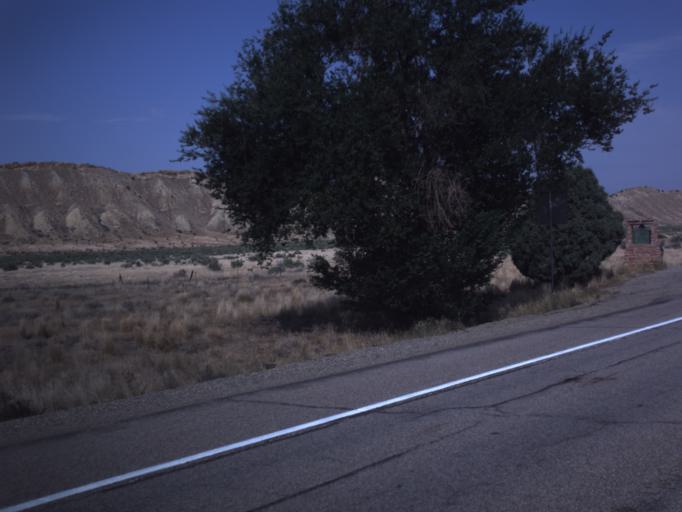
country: US
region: Colorado
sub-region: Rio Blanco County
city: Rangely
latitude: 40.2760
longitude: -109.0546
